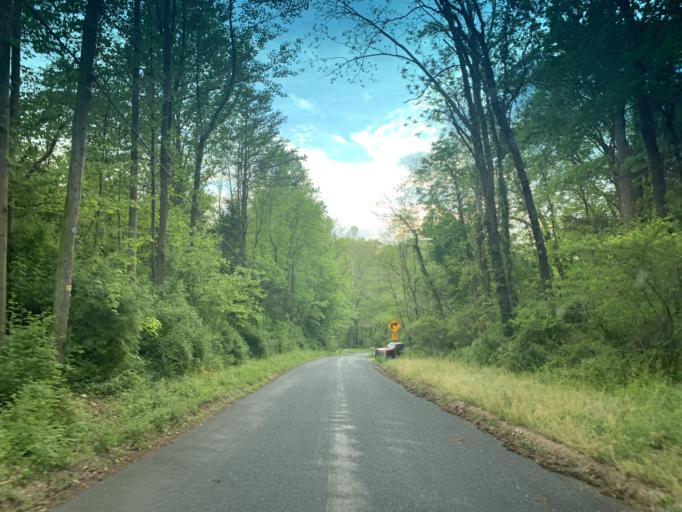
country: US
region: Pennsylvania
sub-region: York County
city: Susquehanna Trails
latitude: 39.6750
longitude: -76.2764
